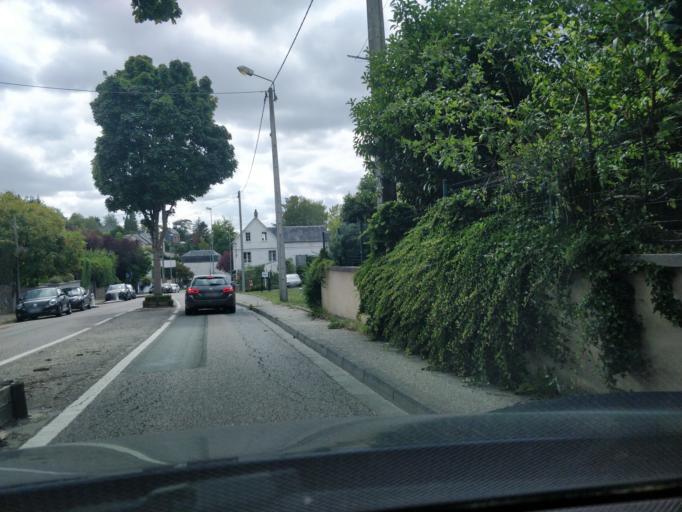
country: FR
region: Haute-Normandie
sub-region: Departement de la Seine-Maritime
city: Mont-Saint-Aignan
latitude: 49.4647
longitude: 1.1002
